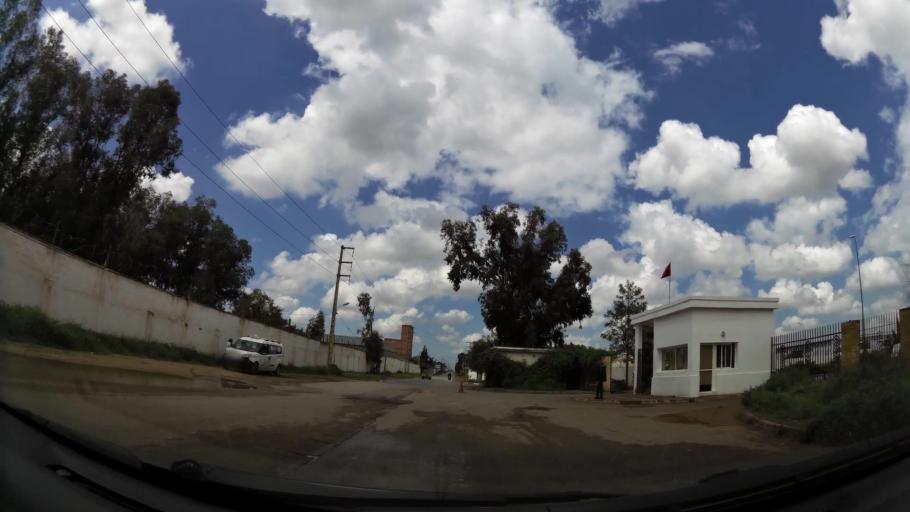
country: MA
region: Chaouia-Ouardigha
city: Nouaseur
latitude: 33.3828
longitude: -7.5745
